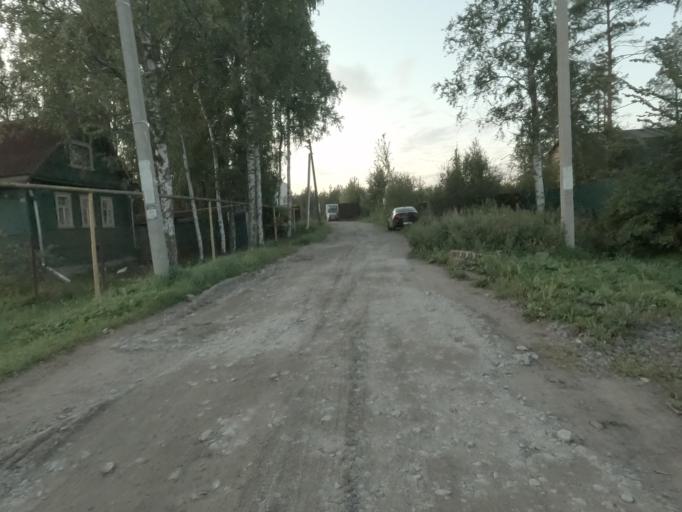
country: RU
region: Leningrad
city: Mga
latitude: 59.7613
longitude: 31.0618
